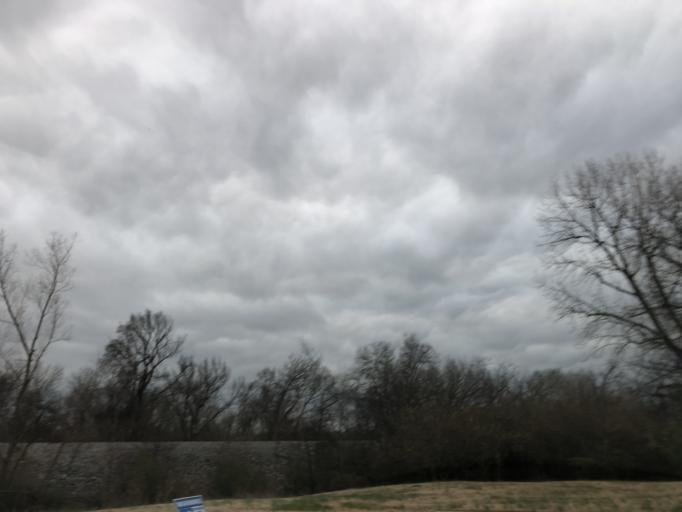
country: US
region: Tennessee
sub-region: Davidson County
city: Goodlettsville
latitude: 36.2920
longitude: -86.6856
